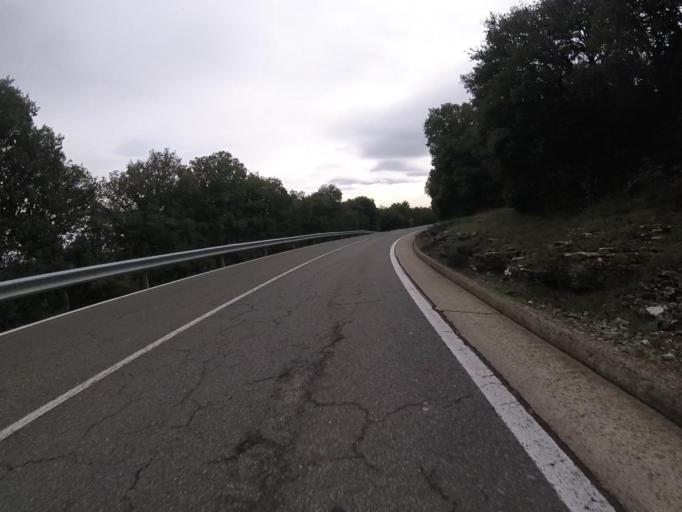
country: ES
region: Navarre
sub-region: Provincia de Navarra
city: Lezaun
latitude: 42.7501
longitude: -2.0139
